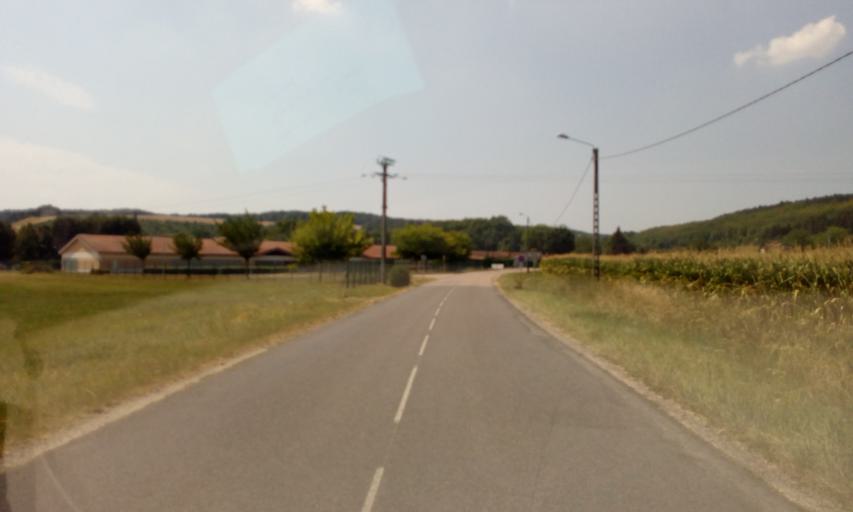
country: FR
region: Lorraine
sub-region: Departement de la Meuse
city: Verdun
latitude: 49.1822
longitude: 5.5008
